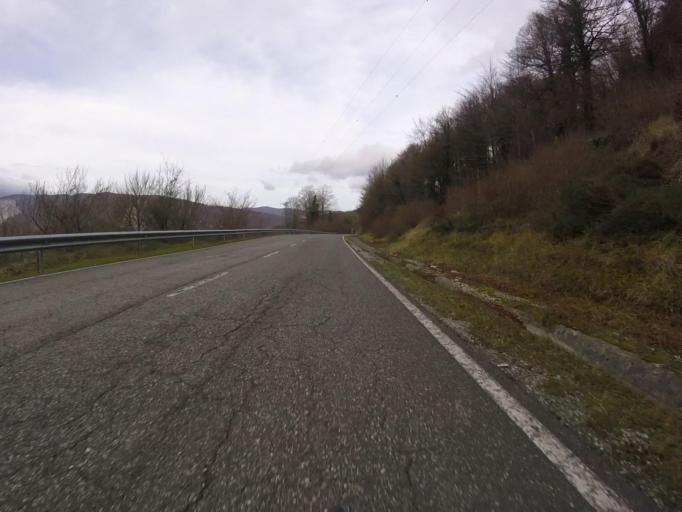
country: ES
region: Navarre
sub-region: Provincia de Navarra
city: Olazagutia
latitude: 42.8624
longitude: -2.1854
